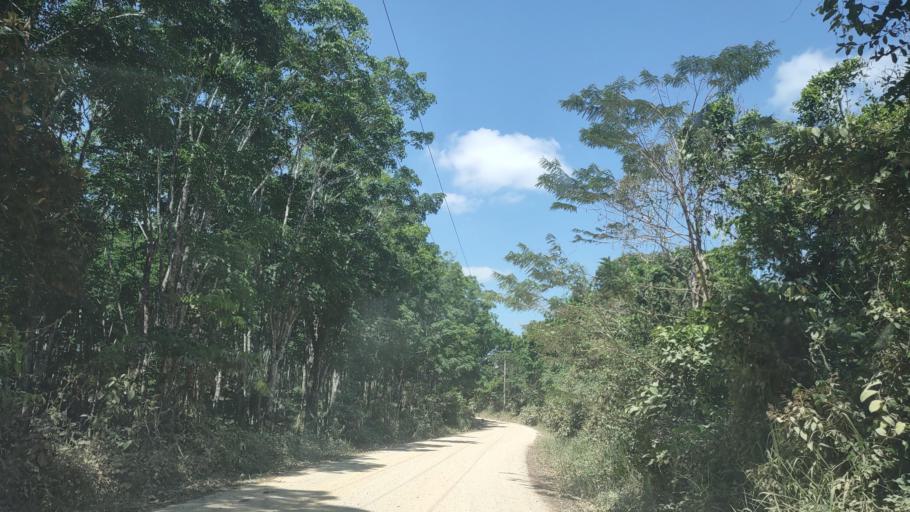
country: MX
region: Veracruz
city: Las Choapas
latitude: 17.7707
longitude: -94.1506
